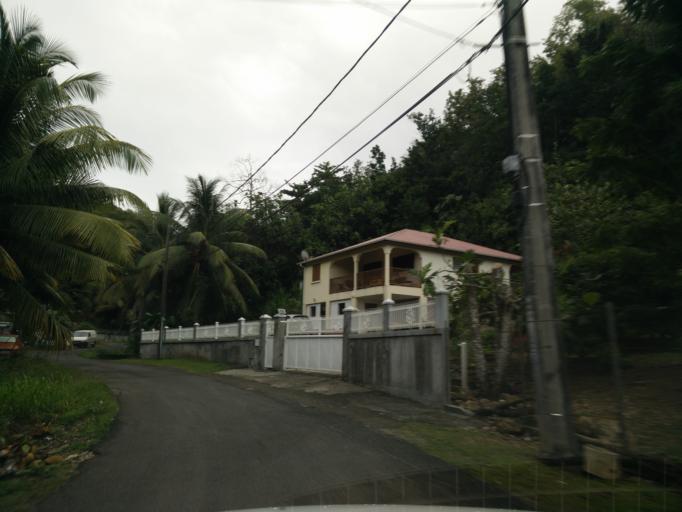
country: GP
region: Guadeloupe
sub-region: Guadeloupe
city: Le Gosier
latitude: 16.2263
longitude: -61.4983
